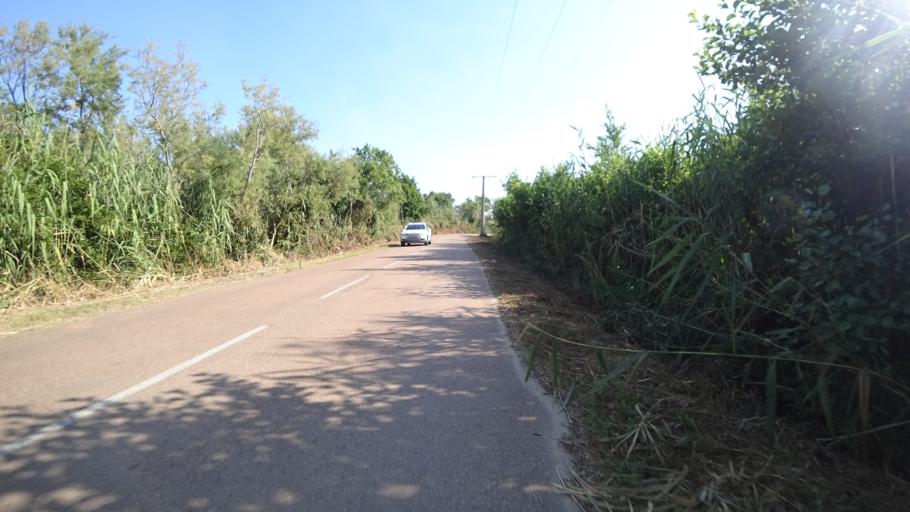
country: FR
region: Corsica
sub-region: Departement de la Corse-du-Sud
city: Porto-Vecchio
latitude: 41.6228
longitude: 9.3340
